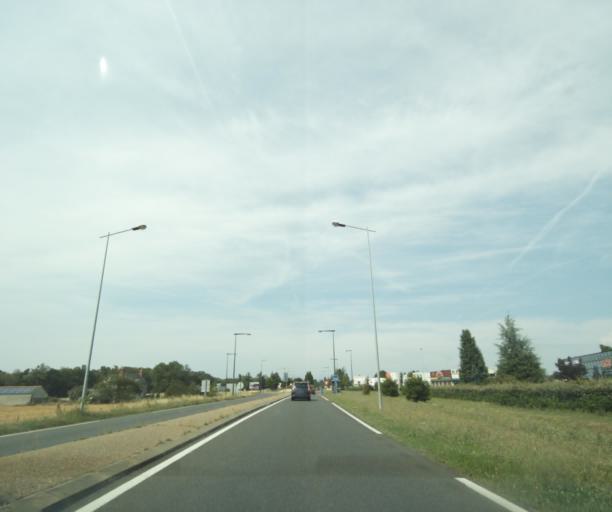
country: FR
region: Centre
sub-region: Departement d'Indre-et-Loire
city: Montbazon
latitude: 47.2739
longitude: 0.7085
